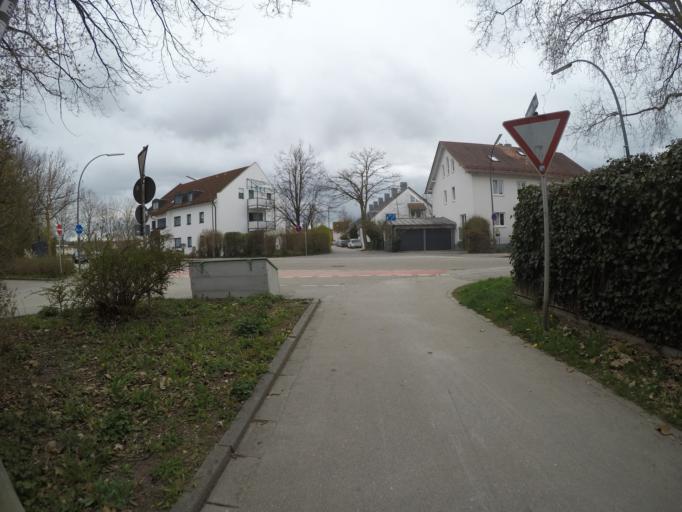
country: DE
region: Bavaria
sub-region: Lower Bavaria
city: Landshut
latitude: 48.5414
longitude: 12.1241
